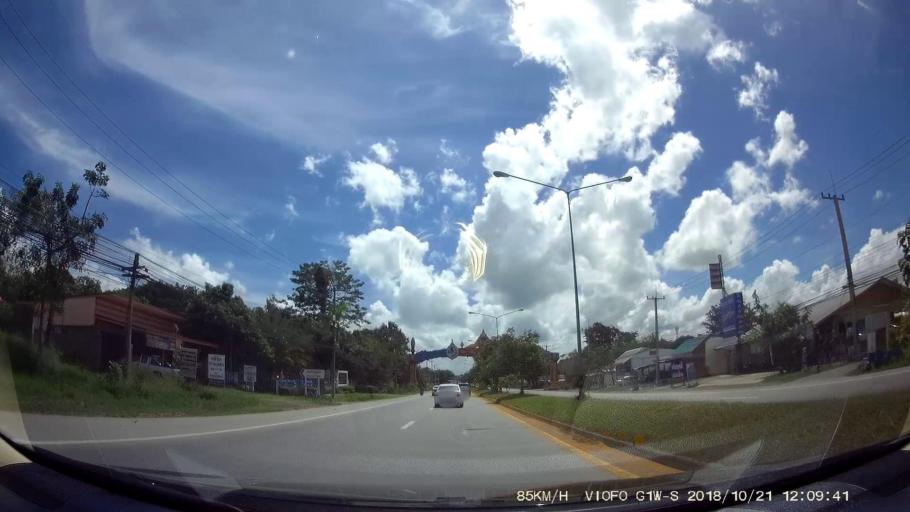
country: TH
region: Chaiyaphum
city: Chatturat
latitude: 15.4180
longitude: 101.8330
